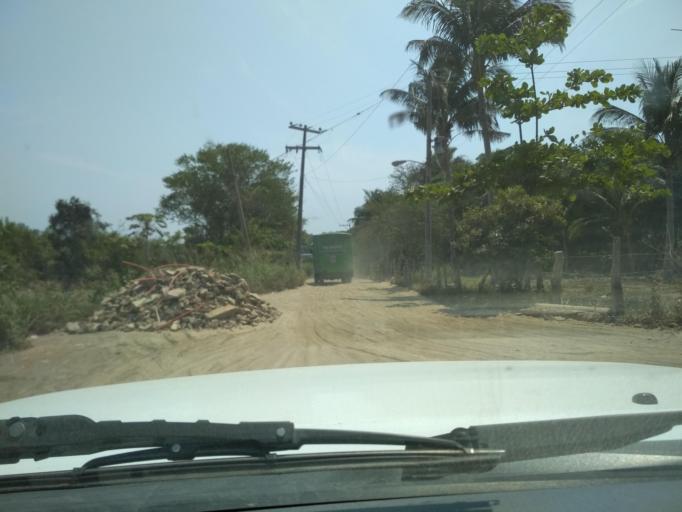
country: MX
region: Veracruz
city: Boca del Rio
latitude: 19.0981
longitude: -96.1244
